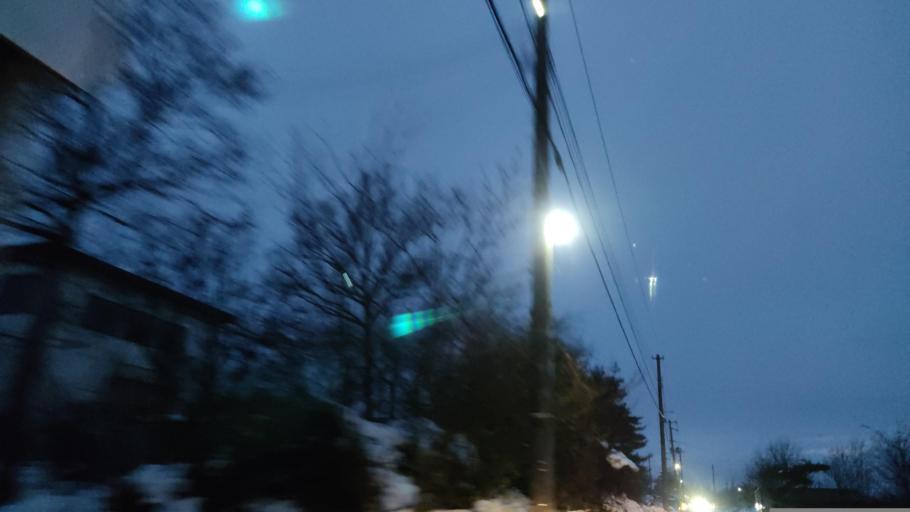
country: JP
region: Iwate
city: Morioka-shi
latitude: 39.6305
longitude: 141.1064
